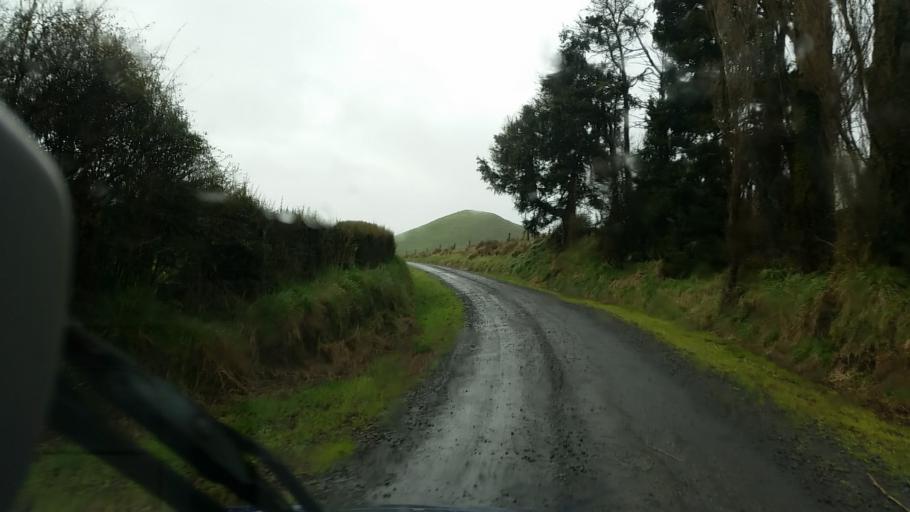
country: NZ
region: Taranaki
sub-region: South Taranaki District
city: Eltham
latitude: -39.3475
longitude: 174.4380
